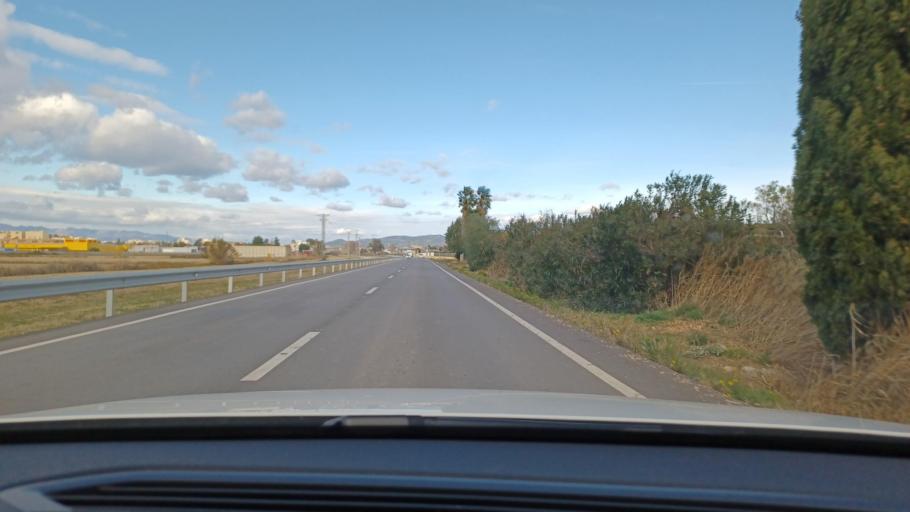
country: ES
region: Catalonia
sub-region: Provincia de Tarragona
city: Amposta
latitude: 40.6979
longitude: 0.5890
